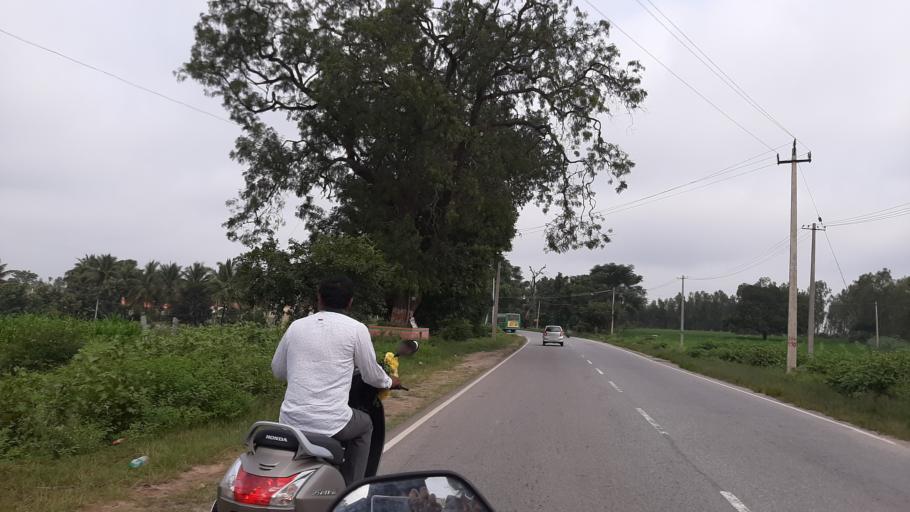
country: IN
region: Karnataka
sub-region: Bangalore Rural
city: Nelamangala
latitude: 12.9686
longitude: 77.3781
